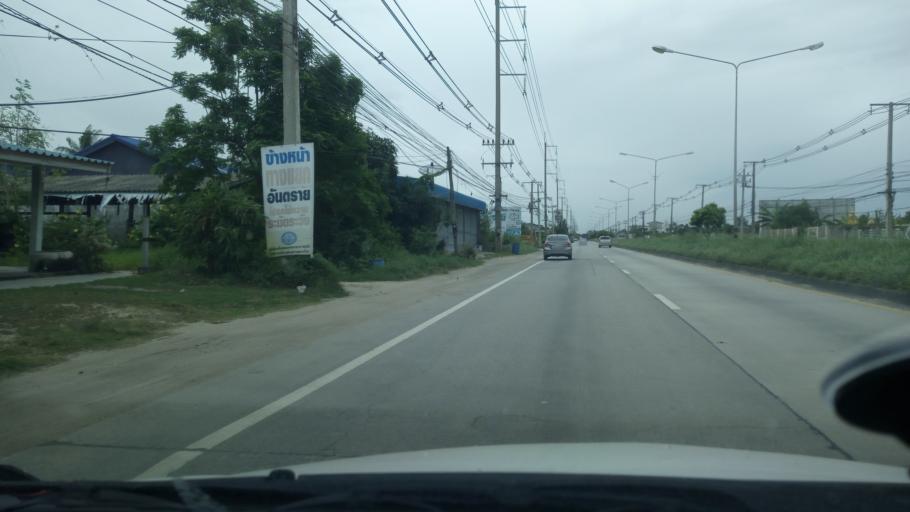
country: TH
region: Chon Buri
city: Phan Thong
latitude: 13.4311
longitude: 101.1282
